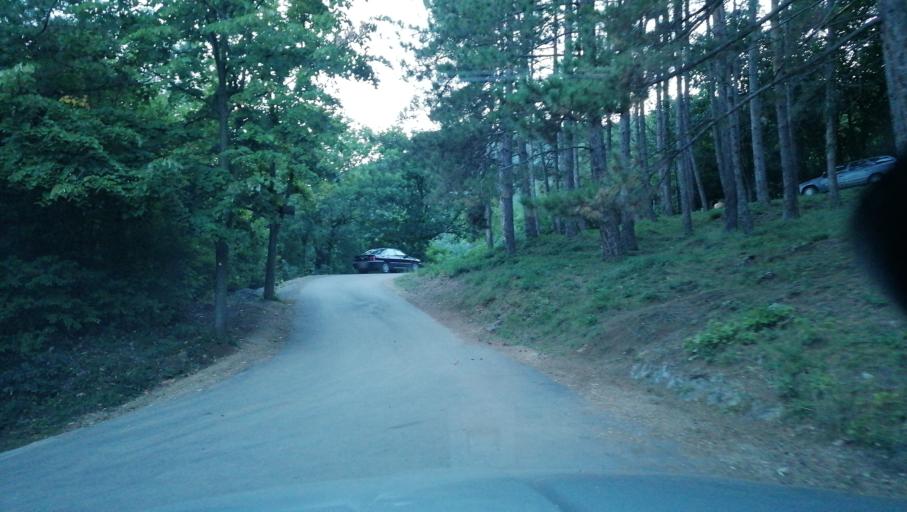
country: RS
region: Central Serbia
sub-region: Kolubarski Okrug
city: Valjevo
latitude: 44.2354
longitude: 19.8656
